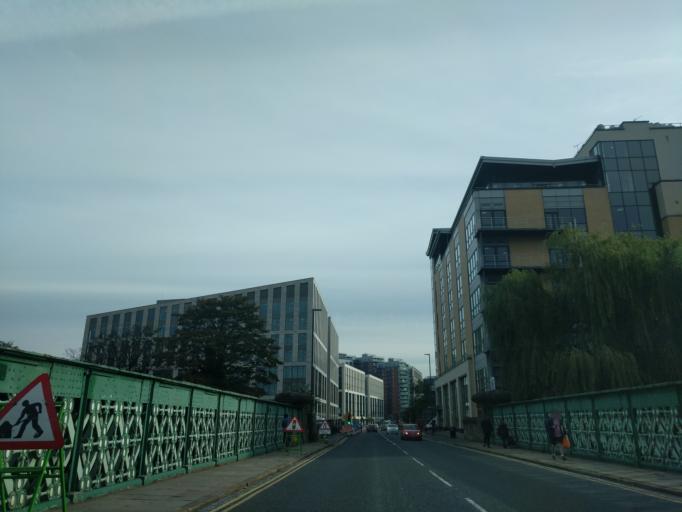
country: GB
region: England
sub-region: City and Borough of Leeds
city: Leeds
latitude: 53.7936
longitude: -1.5589
